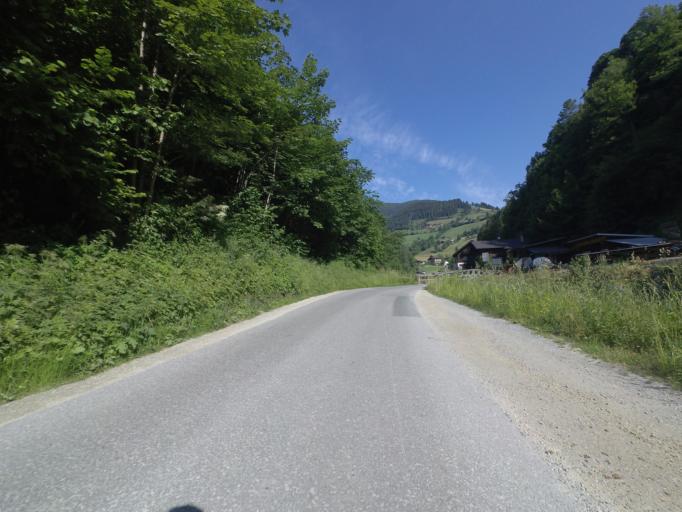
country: AT
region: Salzburg
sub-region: Politischer Bezirk Sankt Johann im Pongau
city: Sankt Veit im Pongau
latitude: 47.3295
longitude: 13.1257
